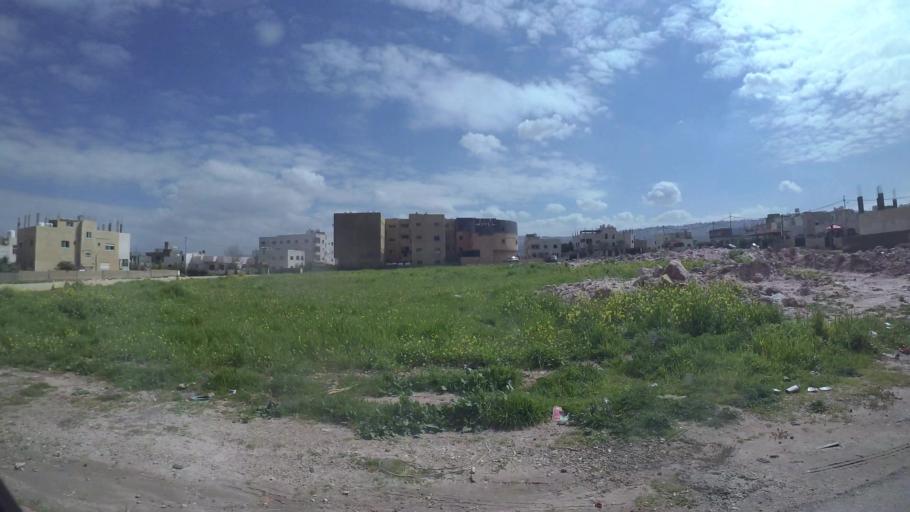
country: JO
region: Amman
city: Al Jubayhah
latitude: 32.0629
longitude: 35.8228
